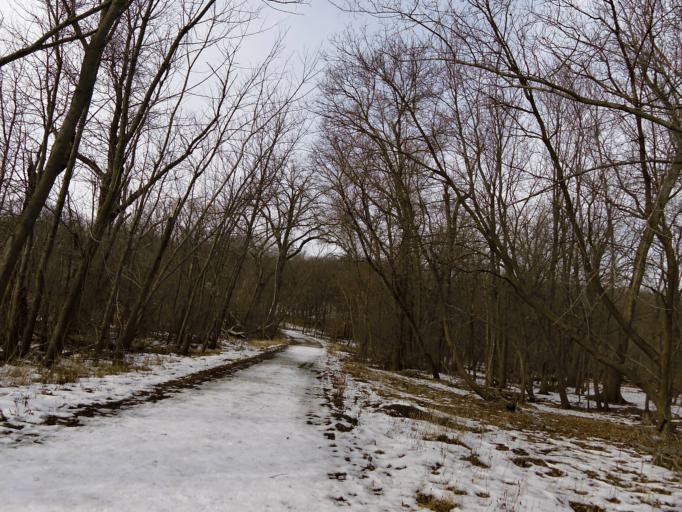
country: US
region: Minnesota
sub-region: Dakota County
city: Eagan
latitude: 44.8570
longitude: -93.2145
